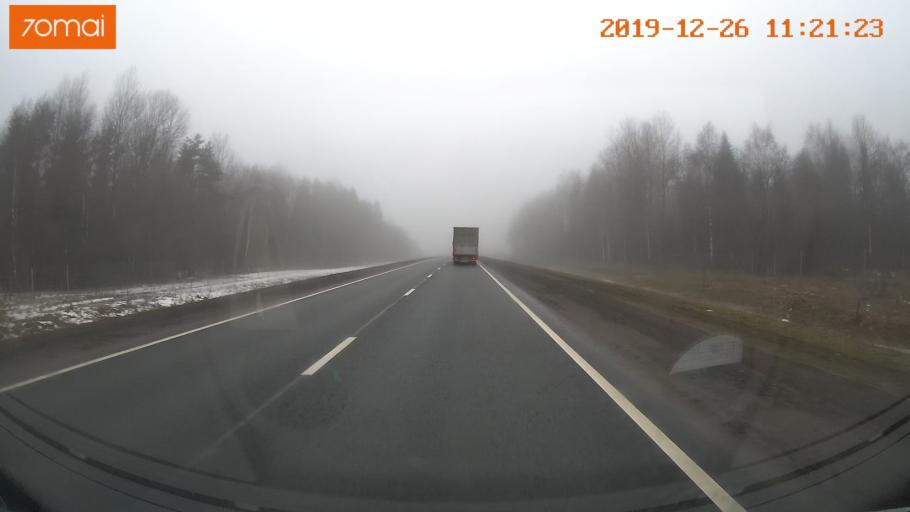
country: RU
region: Vologda
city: Chebsara
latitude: 59.1238
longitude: 38.9660
